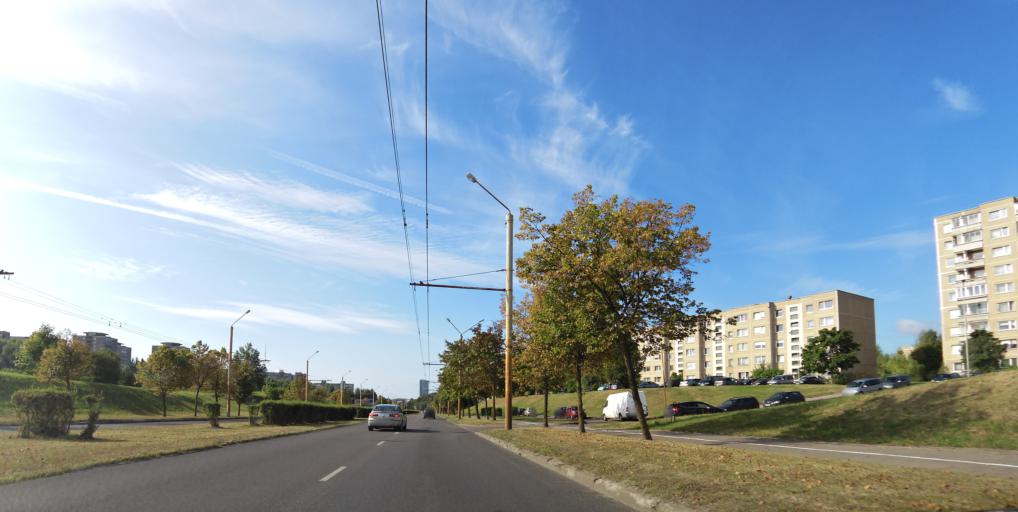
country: LT
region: Vilnius County
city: Justiniskes
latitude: 54.7148
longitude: 25.2197
